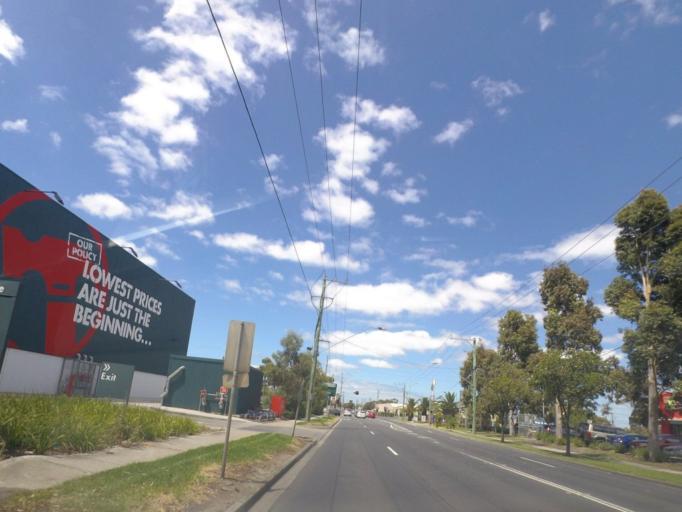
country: AU
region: Victoria
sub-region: Brimbank
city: Sunshine North
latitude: -37.7757
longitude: 144.8290
